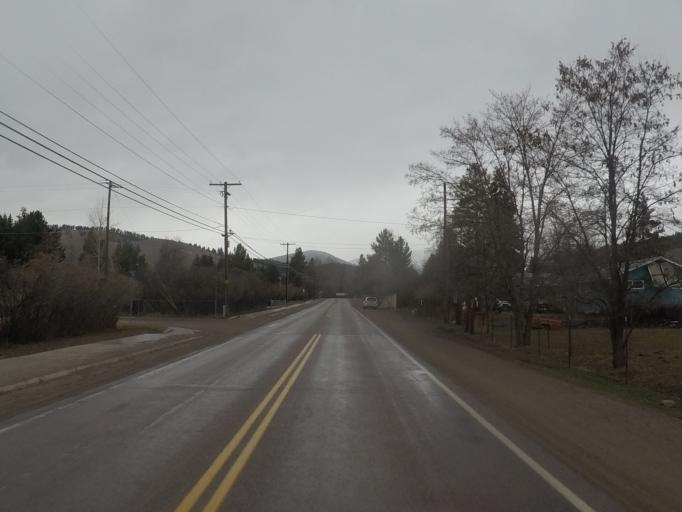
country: US
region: Montana
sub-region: Missoula County
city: East Missoula
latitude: 46.8974
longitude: -113.9656
